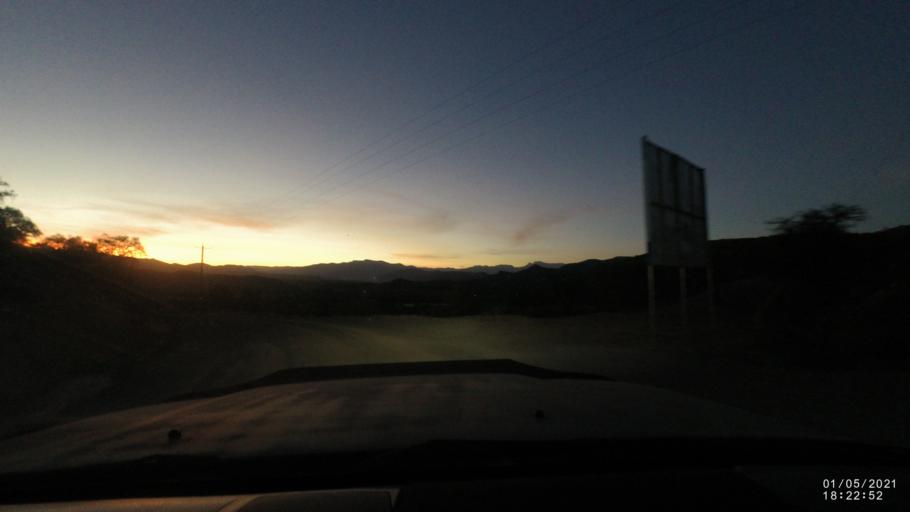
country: BO
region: Cochabamba
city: Capinota
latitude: -17.6587
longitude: -66.2348
